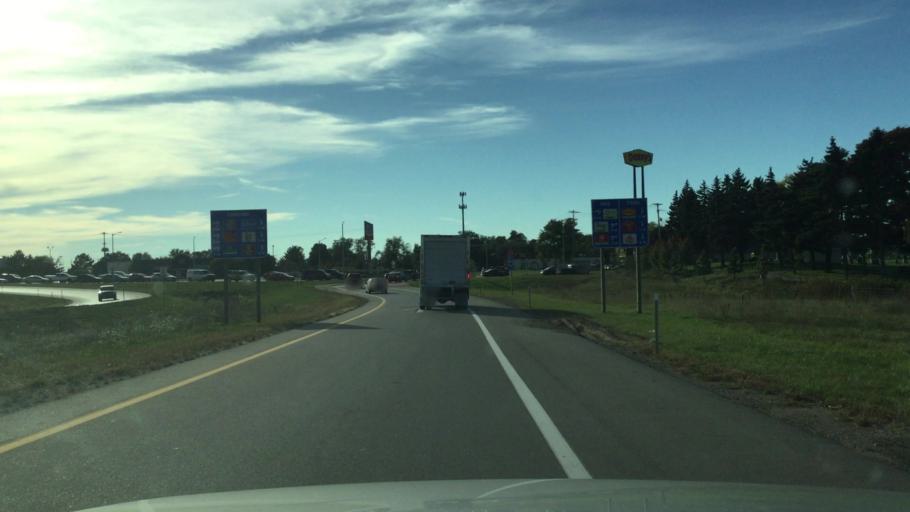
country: US
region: Michigan
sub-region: Kalamazoo County
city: Eastwood
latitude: 42.2625
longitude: -85.5288
